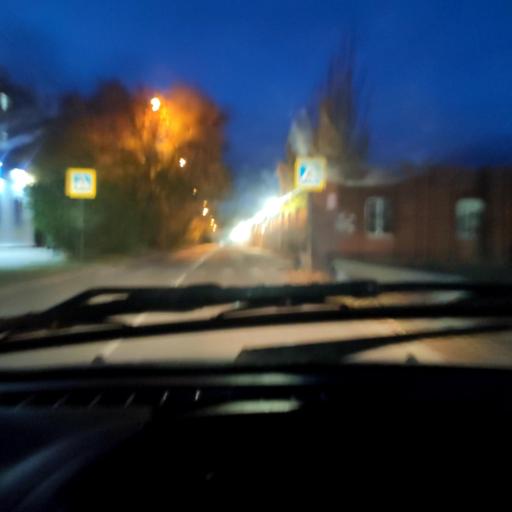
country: RU
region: Samara
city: Zhigulevsk
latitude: 53.4690
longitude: 49.5303
